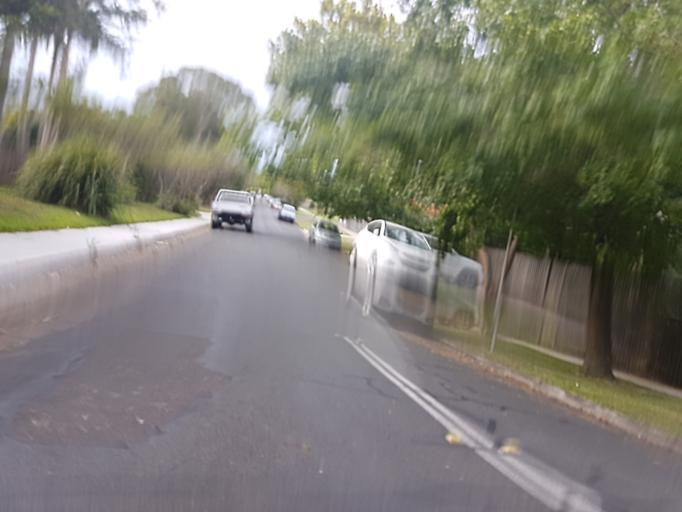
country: AU
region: New South Wales
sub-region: Willoughby
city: Castle Cove
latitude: -33.7989
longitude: 151.2049
